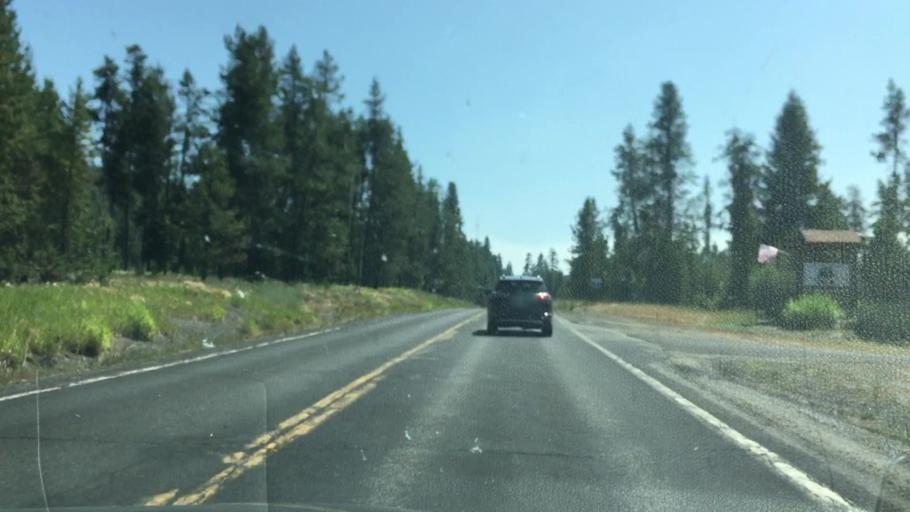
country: US
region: Idaho
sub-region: Valley County
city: McCall
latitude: 44.9496
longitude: -116.1687
